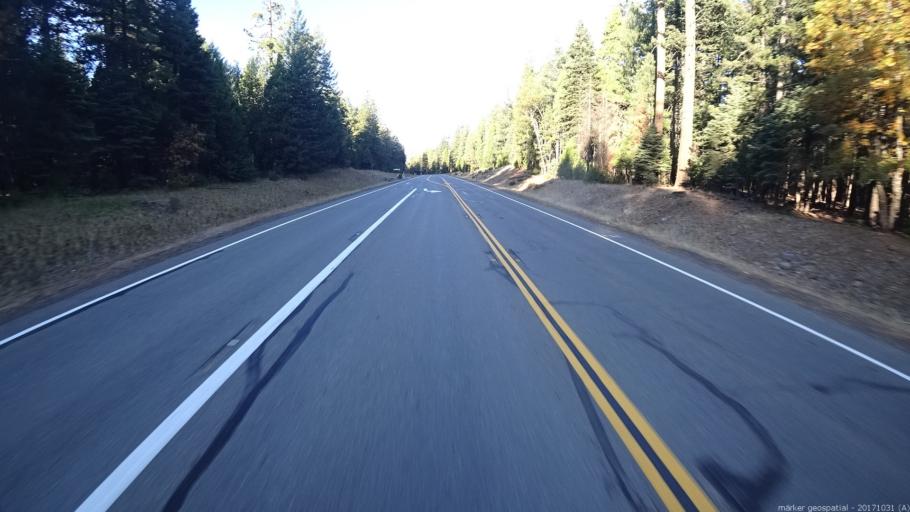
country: US
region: California
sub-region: Shasta County
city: Shingletown
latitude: 40.5175
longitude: -121.7943
